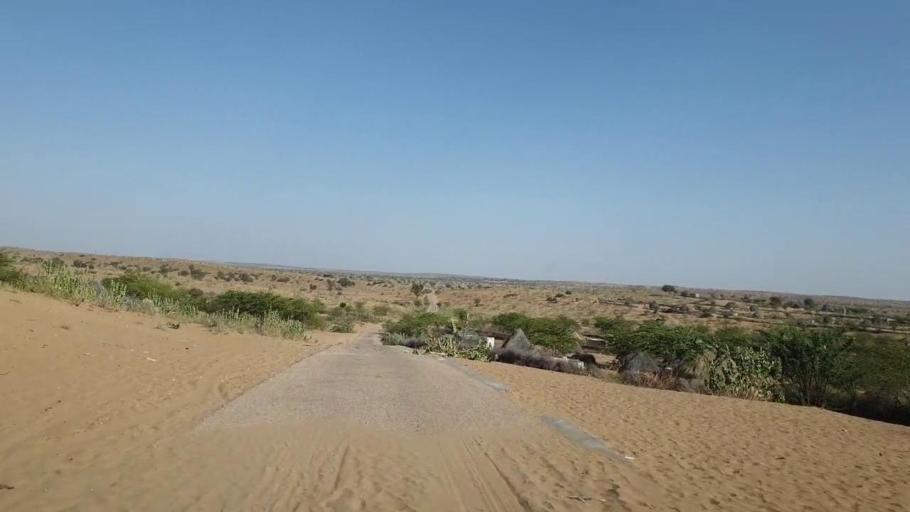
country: PK
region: Sindh
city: Islamkot
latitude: 25.0382
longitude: 70.0225
